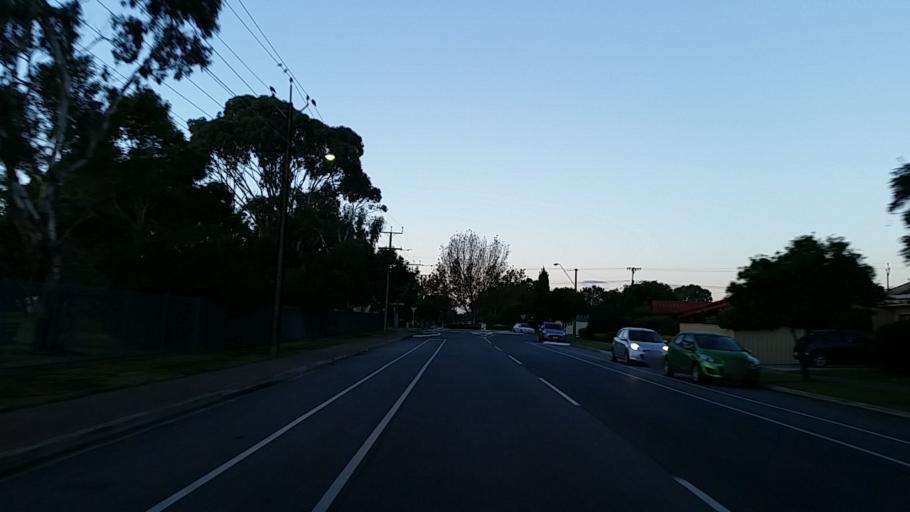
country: AU
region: South Australia
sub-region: Charles Sturt
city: Henley Beach
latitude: -34.9155
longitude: 138.5003
